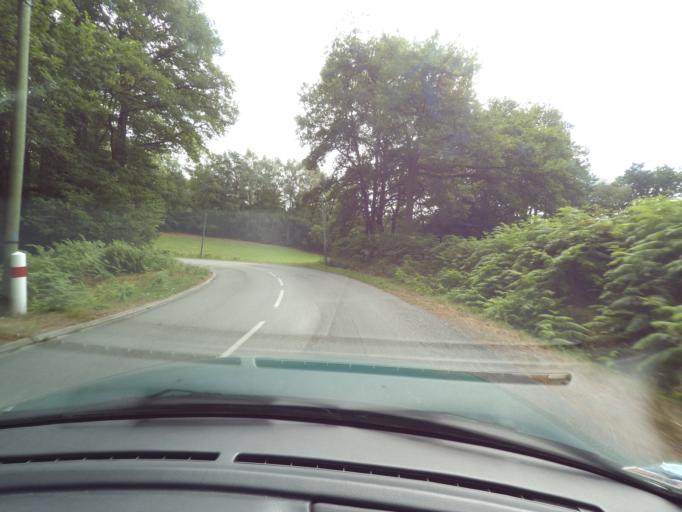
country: FR
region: Limousin
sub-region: Departement de la Haute-Vienne
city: Eymoutiers
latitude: 45.7190
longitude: 1.8637
